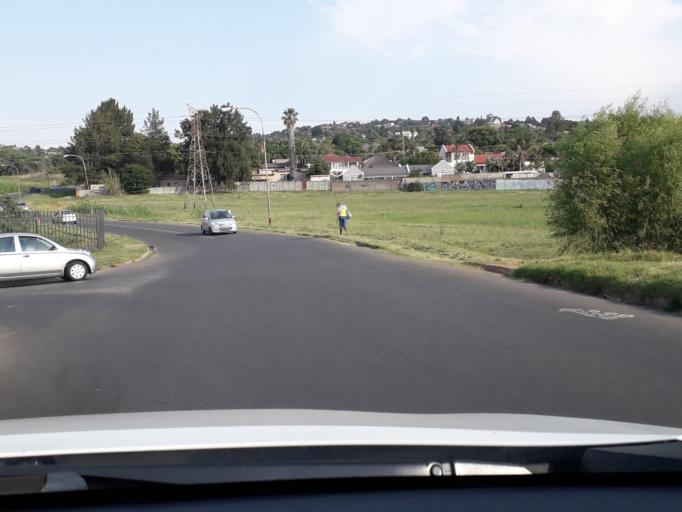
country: ZA
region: Gauteng
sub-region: City of Johannesburg Metropolitan Municipality
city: Johannesburg
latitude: -26.1592
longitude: 27.9763
